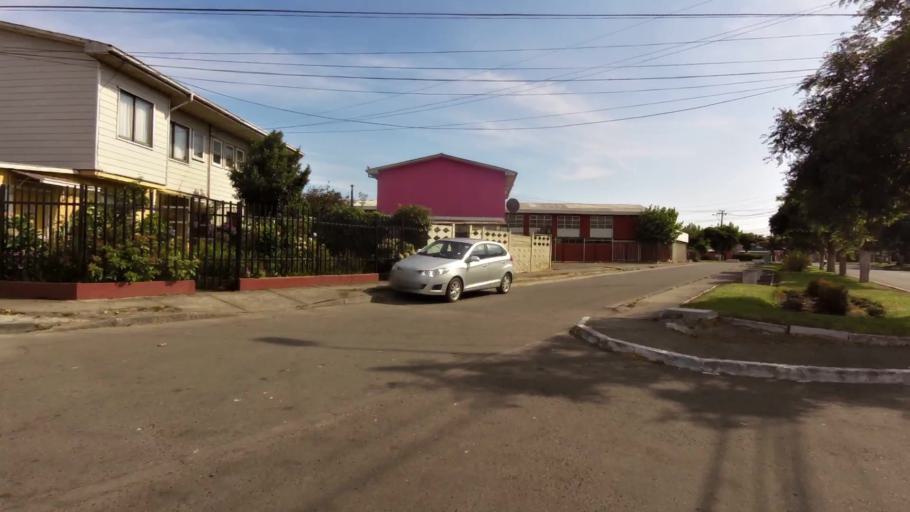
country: CL
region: Biobio
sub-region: Provincia de Concepcion
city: Talcahuano
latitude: -36.7876
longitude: -73.1070
